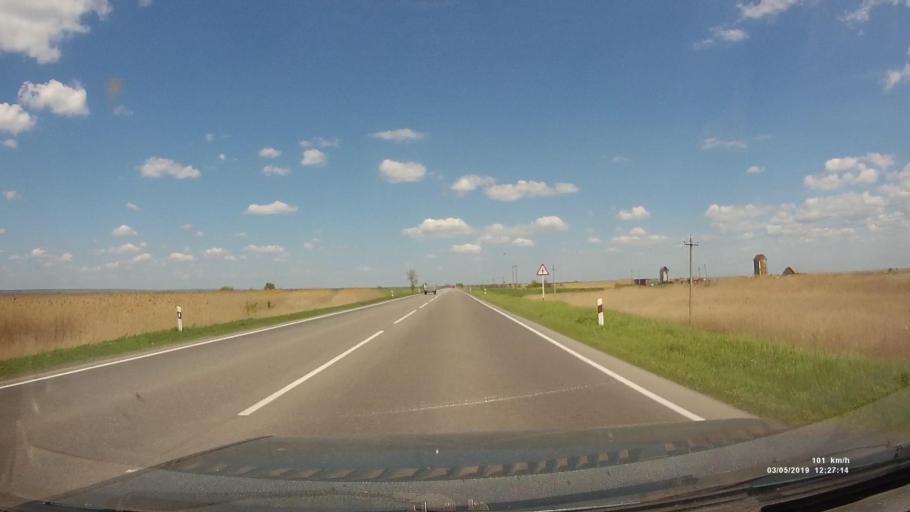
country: RU
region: Rostov
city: Semikarakorsk
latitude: 47.4569
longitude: 40.7197
